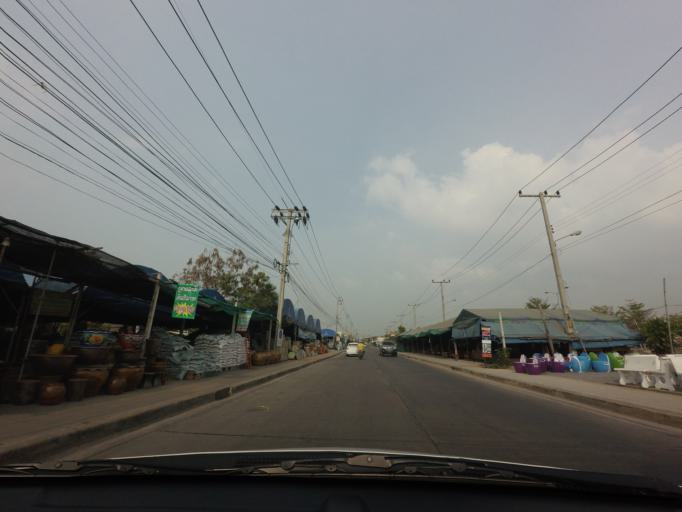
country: TH
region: Bangkok
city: Nong Khaem
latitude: 13.7426
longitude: 100.3502
